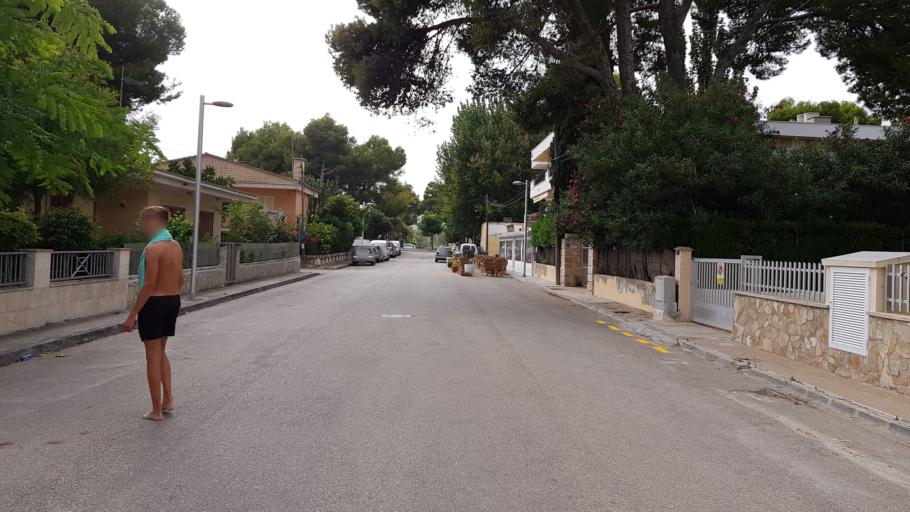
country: ES
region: Balearic Islands
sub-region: Illes Balears
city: Port d'Alcudia
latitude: 39.8190
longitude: 3.1159
